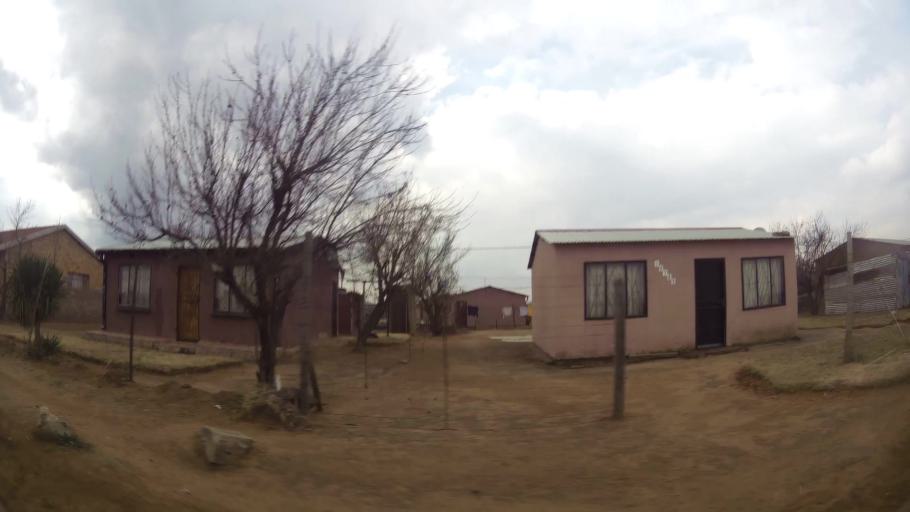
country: ZA
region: Orange Free State
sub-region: Fezile Dabi District Municipality
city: Sasolburg
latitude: -26.8630
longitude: 27.8765
